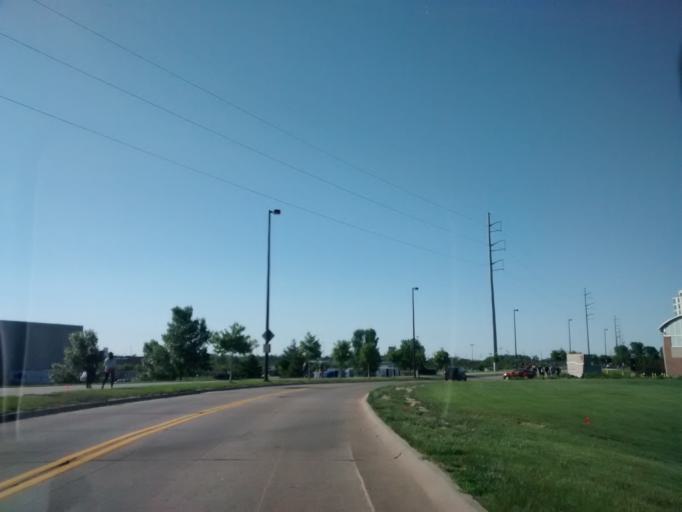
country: US
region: Nebraska
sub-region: Douglas County
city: Omaha
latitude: 41.2638
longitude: -95.9257
